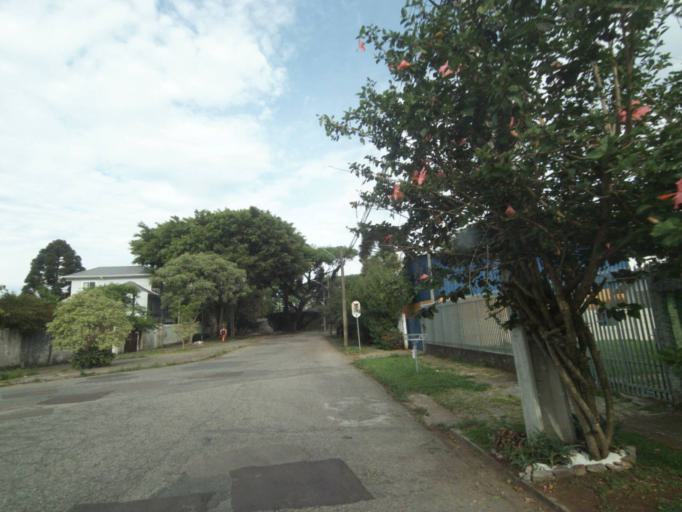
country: BR
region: Parana
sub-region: Curitiba
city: Curitiba
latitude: -25.4293
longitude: -49.2326
